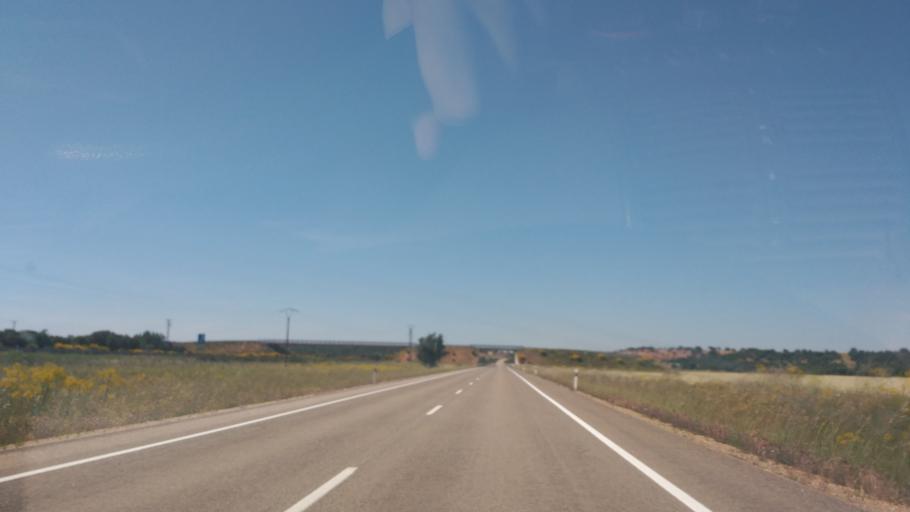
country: ES
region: Castille and Leon
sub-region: Provincia de Salamanca
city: Topas
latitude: 41.2072
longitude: -5.7008
